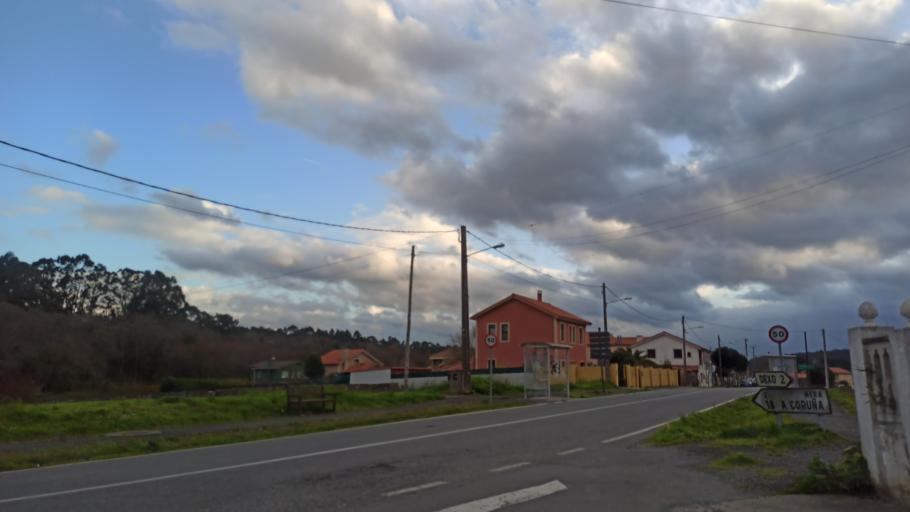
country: ES
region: Galicia
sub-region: Provincia da Coruna
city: Oleiros
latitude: 43.3864
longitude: -8.3215
